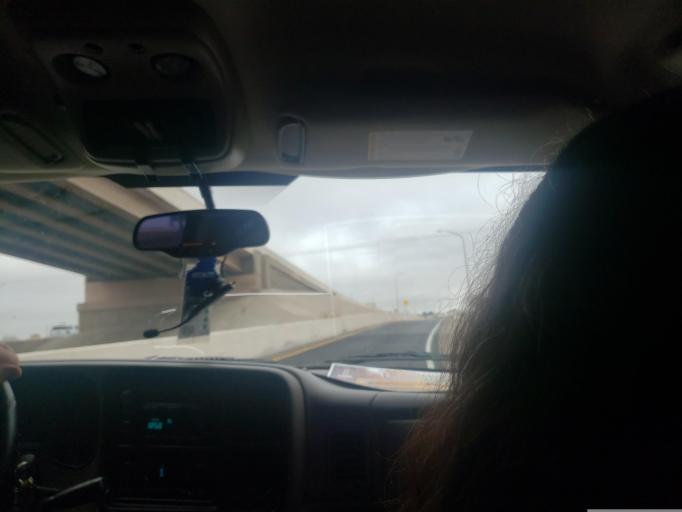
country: US
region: New Mexico
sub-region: Bernalillo County
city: Albuquerque
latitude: 35.1086
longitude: -106.7030
